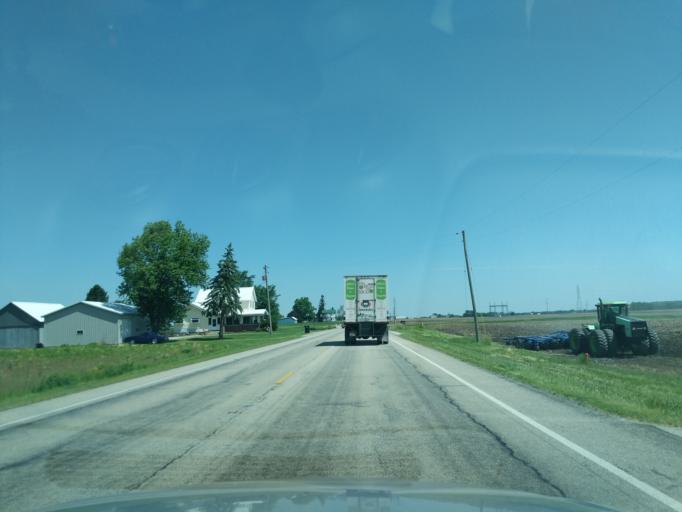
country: US
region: Indiana
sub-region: Whitley County
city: Columbia City
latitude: 41.0541
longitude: -85.4706
